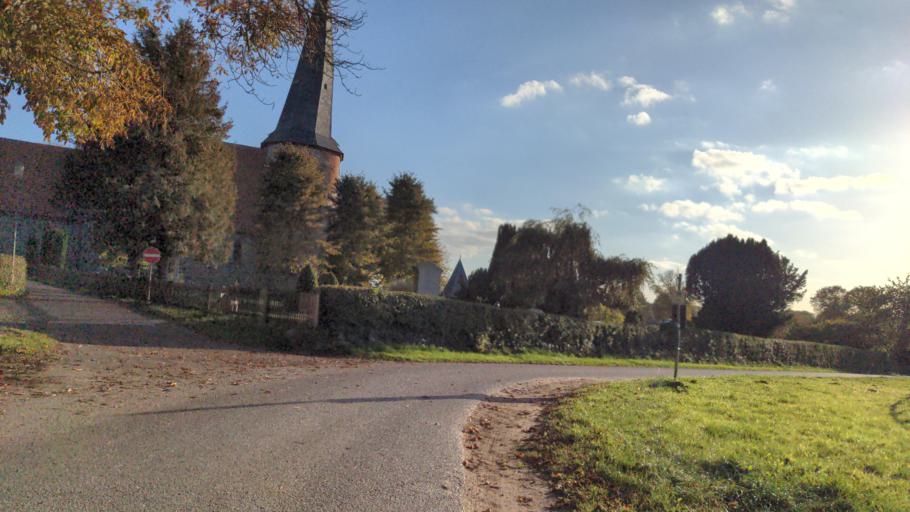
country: DE
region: Schleswig-Holstein
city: Pronstorf
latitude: 53.9589
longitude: 10.4713
